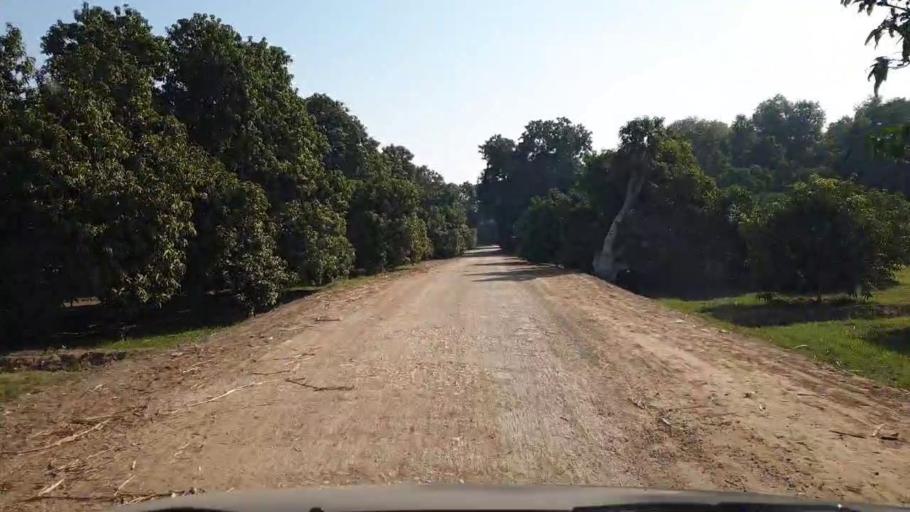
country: PK
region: Sindh
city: Tando Jam
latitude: 25.4353
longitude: 68.6051
